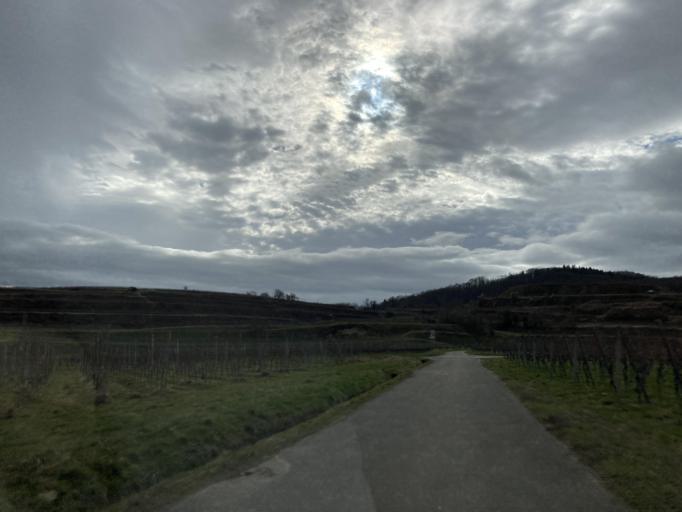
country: DE
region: Baden-Wuerttemberg
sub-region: Freiburg Region
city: Endingen
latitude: 48.1308
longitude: 7.7043
